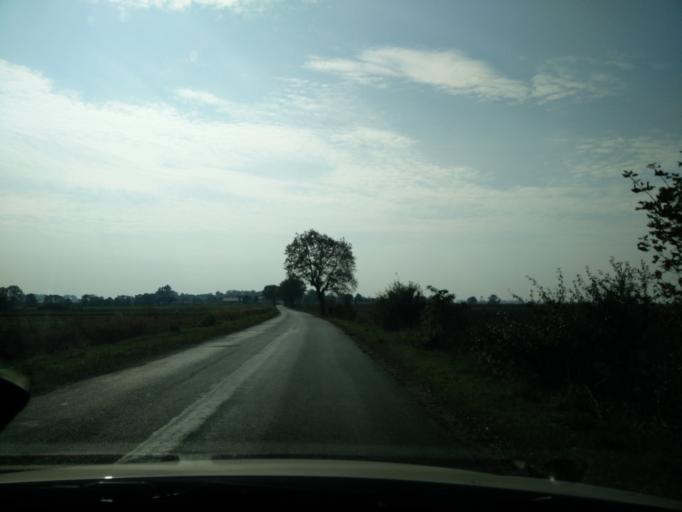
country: PL
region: Greater Poland Voivodeship
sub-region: Powiat sredzki
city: Dominowo
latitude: 52.2735
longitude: 17.3174
